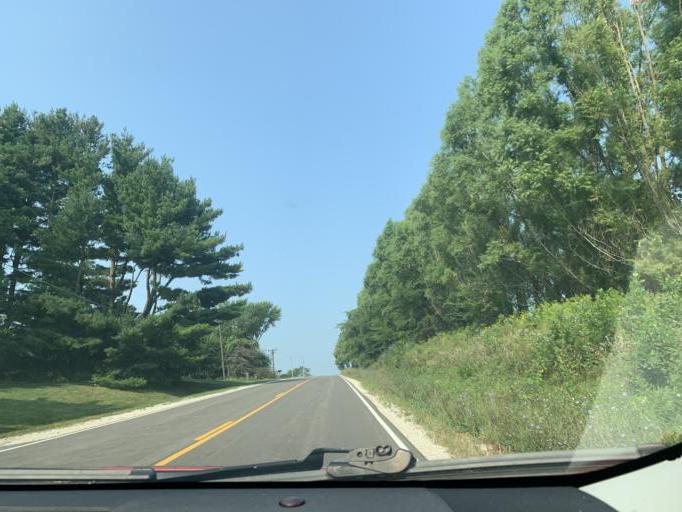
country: US
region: Illinois
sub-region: Whiteside County
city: Sterling
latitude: 41.8441
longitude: -89.7835
